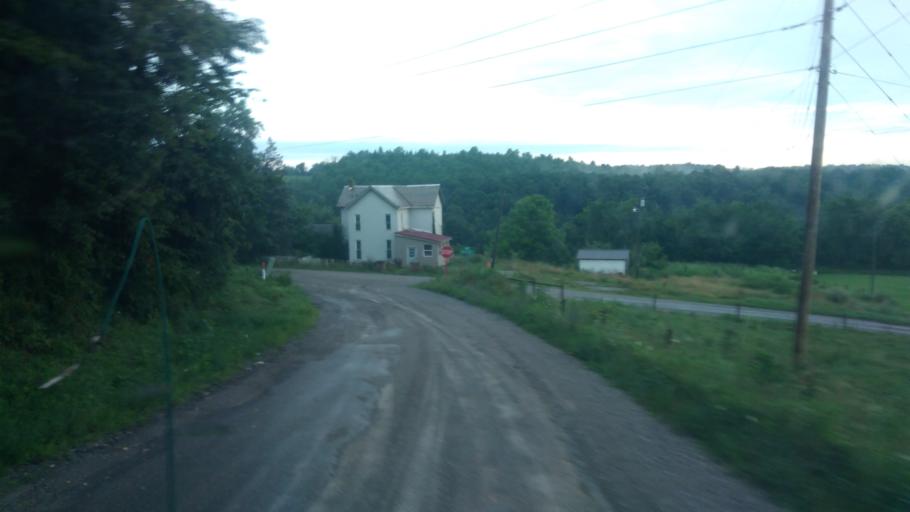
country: US
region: Ohio
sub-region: Guernsey County
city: Byesville
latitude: 40.0217
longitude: -81.3666
